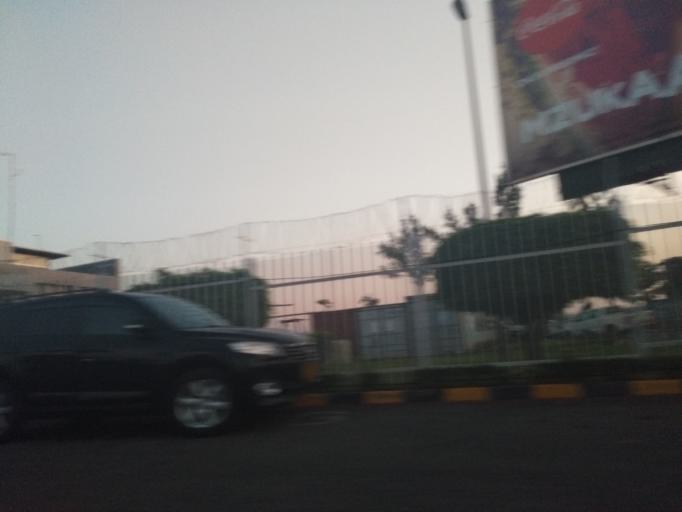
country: TZ
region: Dar es Salaam
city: Dar es Salaam
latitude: -6.8664
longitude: 39.2066
